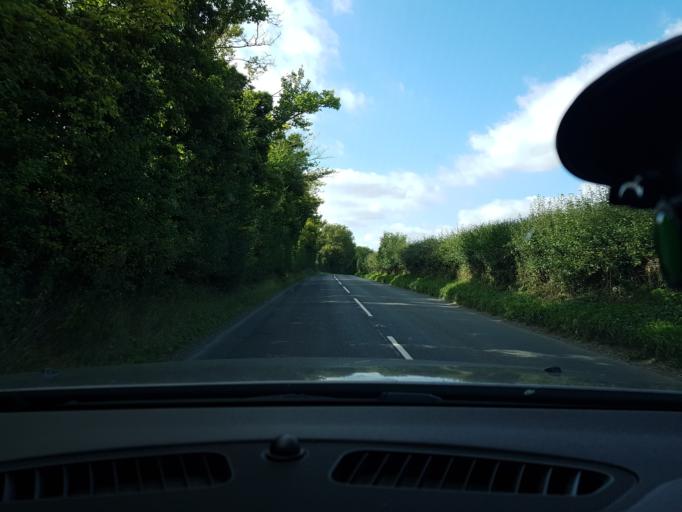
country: GB
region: England
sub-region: Wiltshire
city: Chilton Foliat
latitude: 51.4342
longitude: -1.5535
